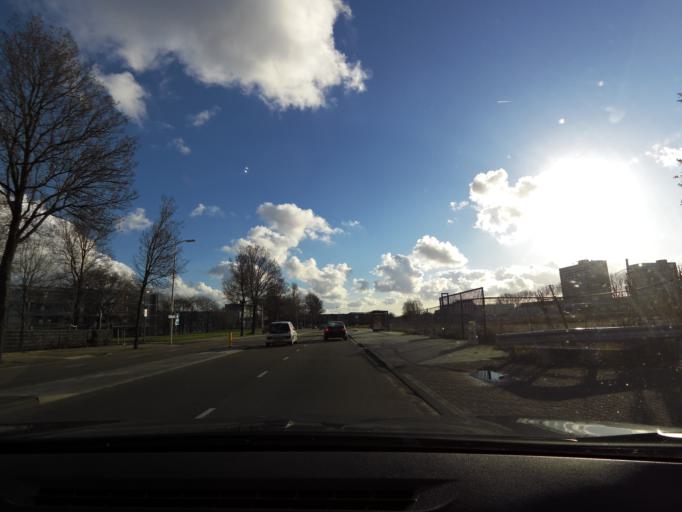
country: NL
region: South Holland
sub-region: Gemeente Den Haag
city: The Hague
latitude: 52.0589
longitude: 4.3121
